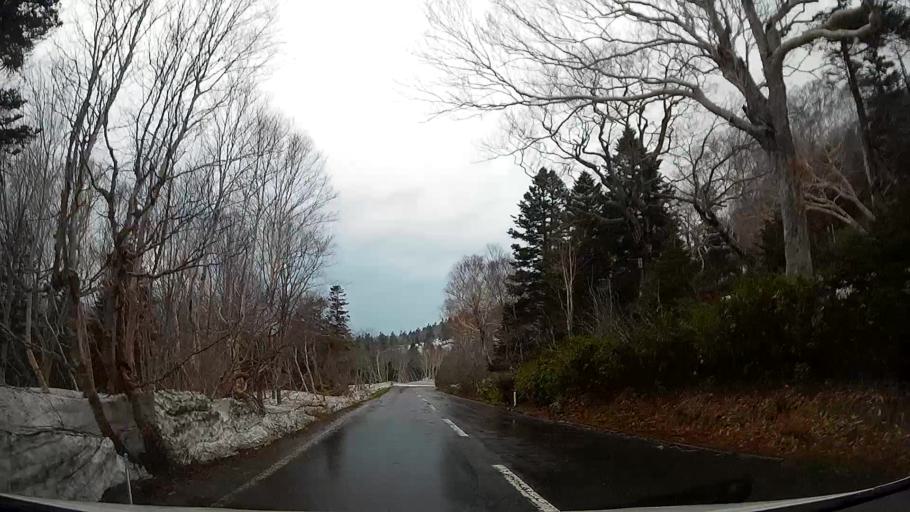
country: JP
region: Aomori
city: Aomori Shi
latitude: 40.6354
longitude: 140.8746
